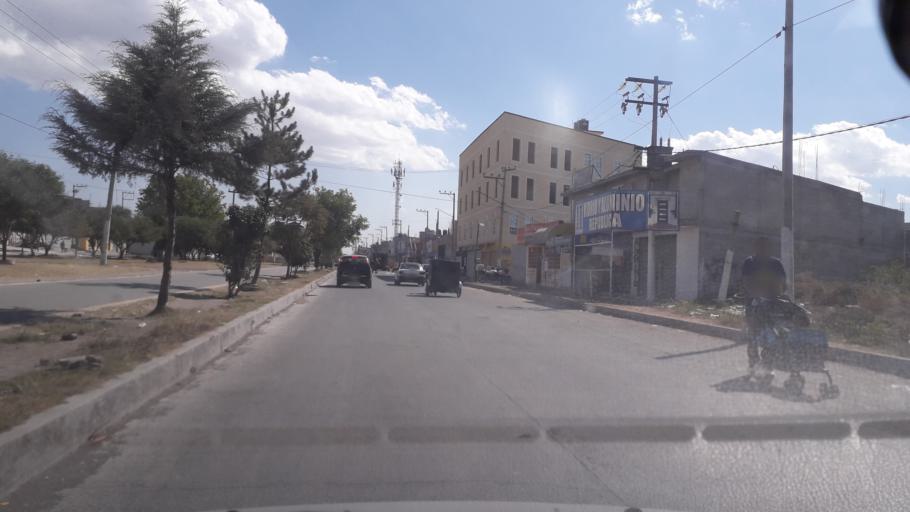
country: MX
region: Mexico
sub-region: Jaltenco
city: Alborada Jaltenco
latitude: 19.6574
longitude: -99.0688
